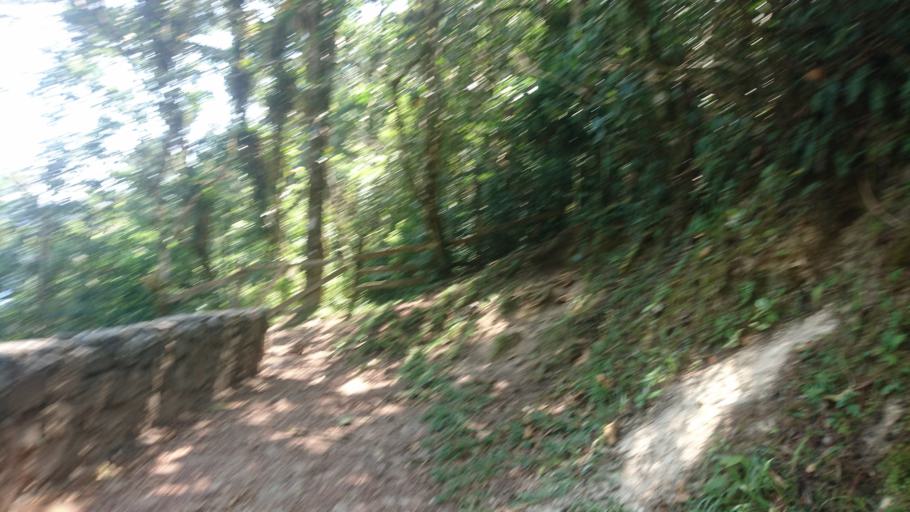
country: GT
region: Huehuetenango
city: Union
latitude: 16.1017
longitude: -91.6689
